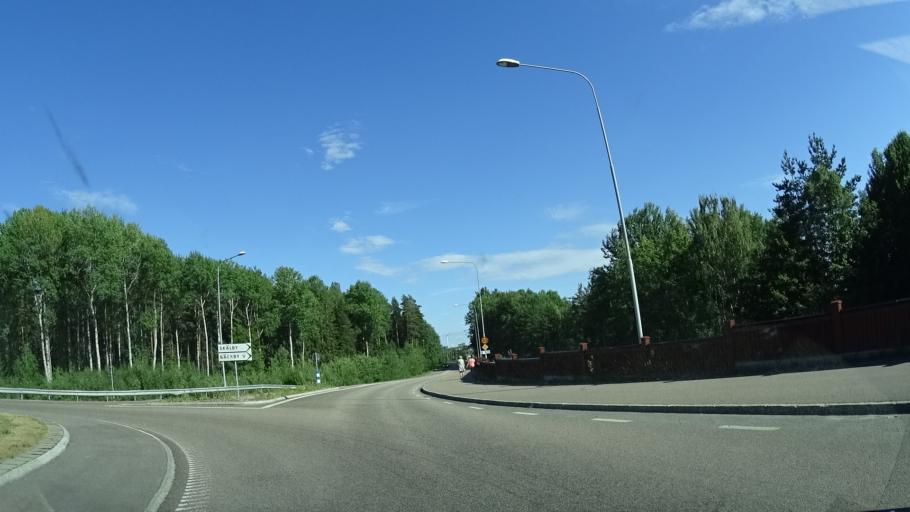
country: SE
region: Vaestmanland
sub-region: Vasteras
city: Vasteras
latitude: 59.6041
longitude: 16.4534
